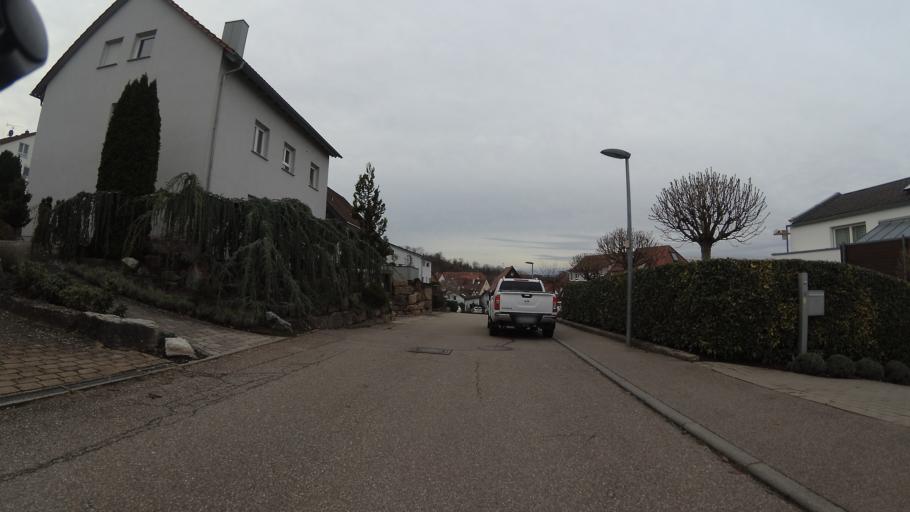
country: DE
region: Baden-Wuerttemberg
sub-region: Regierungsbezirk Stuttgart
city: Oedheim
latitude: 49.2385
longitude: 9.2544
